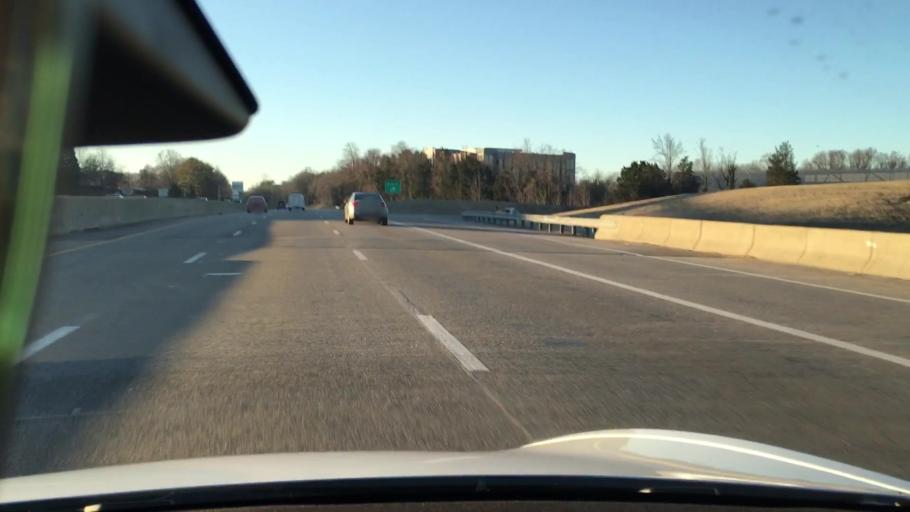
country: US
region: Virginia
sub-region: Chesterfield County
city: Bon Air
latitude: 37.5161
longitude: -77.5284
